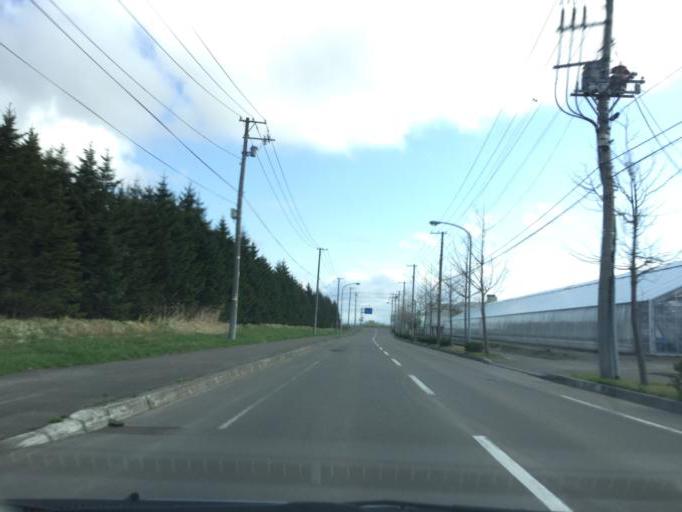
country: JP
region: Hokkaido
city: Ebetsu
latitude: 43.1200
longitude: 141.5407
